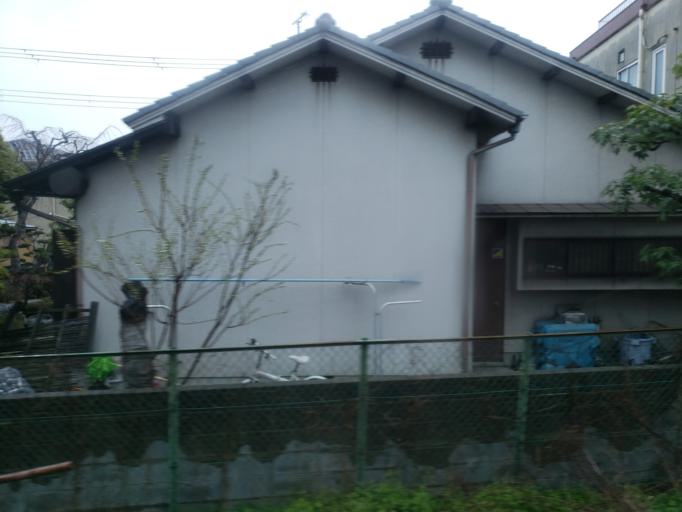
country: JP
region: Hyogo
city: Himeji
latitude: 34.8033
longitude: 134.6731
